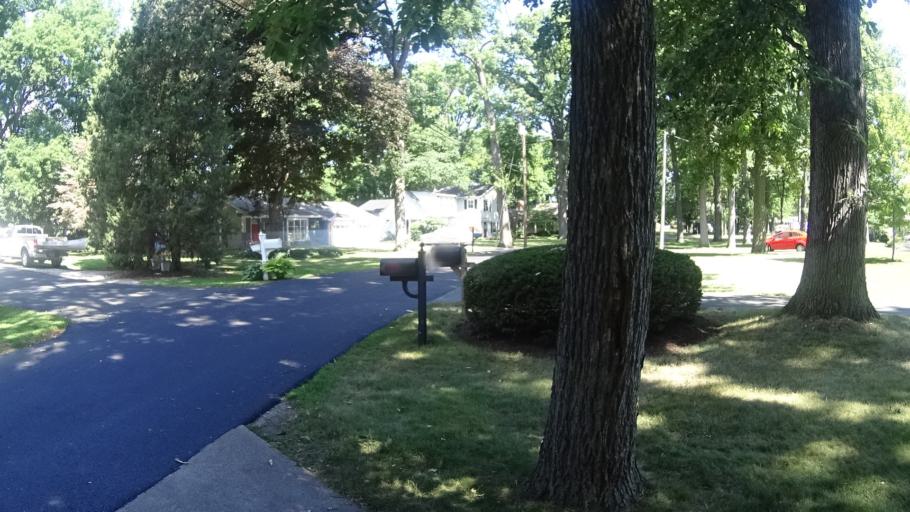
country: US
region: Ohio
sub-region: Erie County
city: Sandusky
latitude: 41.4101
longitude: -82.6540
